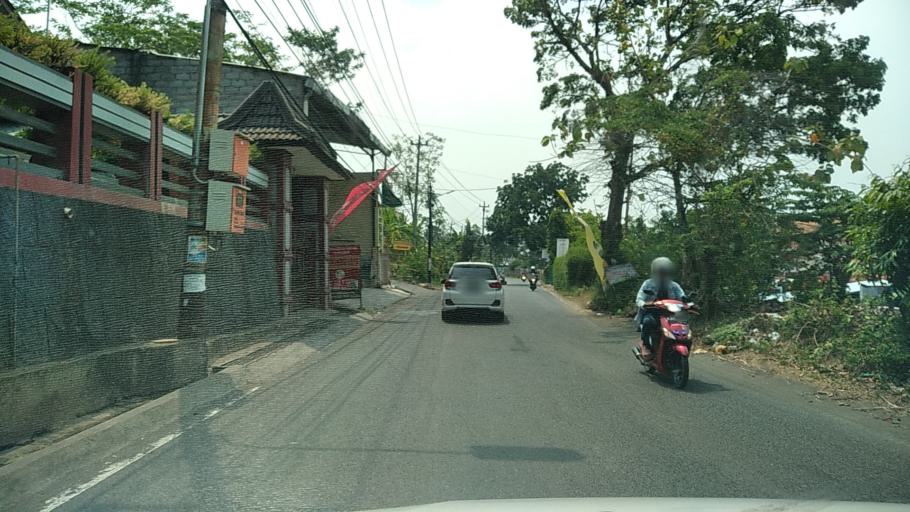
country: ID
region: Central Java
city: Semarang
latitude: -6.9977
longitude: 110.3409
